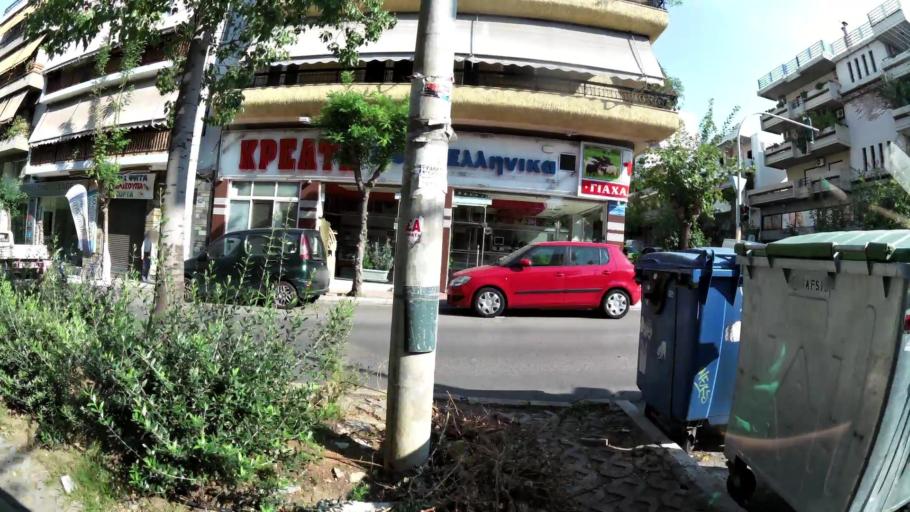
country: GR
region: Attica
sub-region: Nomarchia Athinas
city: Galatsi
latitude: 38.0234
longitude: 23.7478
